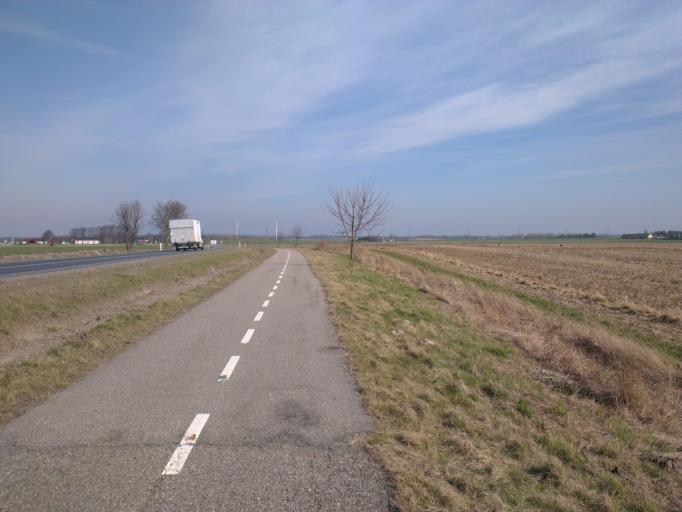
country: DK
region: Capital Region
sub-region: Frederikssund Kommune
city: Skibby
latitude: 55.7862
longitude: 11.9745
